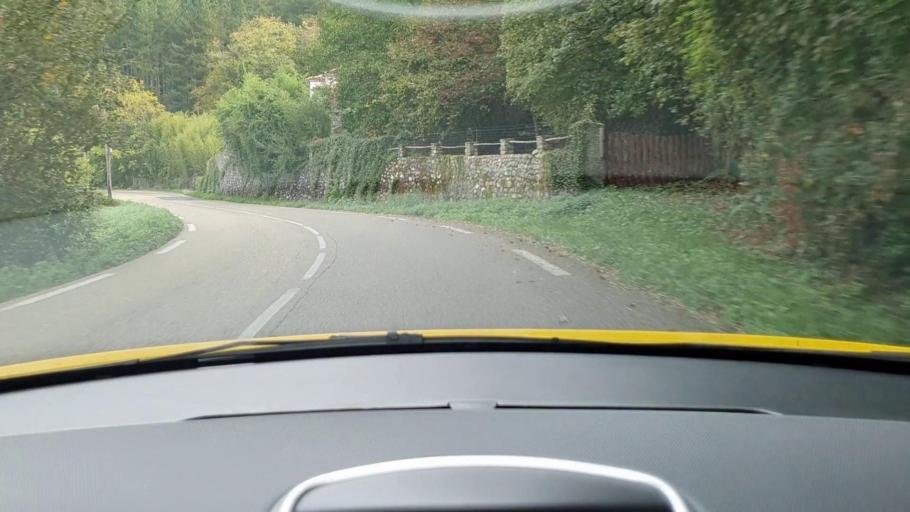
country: FR
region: Languedoc-Roussillon
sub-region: Departement du Gard
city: Le Vigan
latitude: 43.9827
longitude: 3.5859
